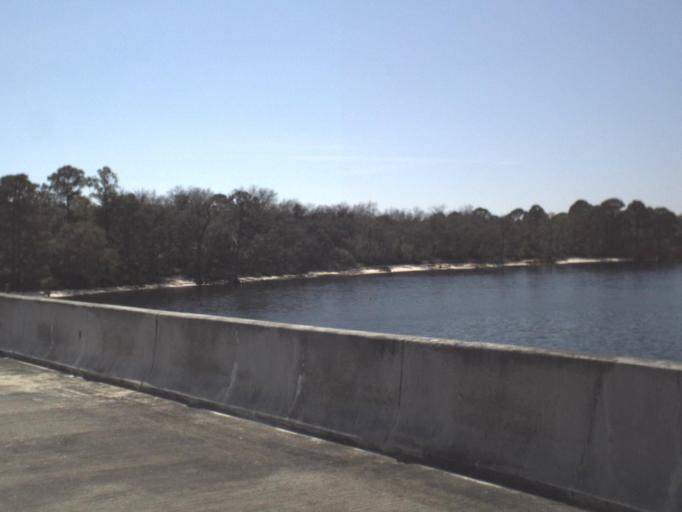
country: US
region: Florida
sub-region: Wakulla County
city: Crawfordville
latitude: 29.9623
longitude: -84.3845
